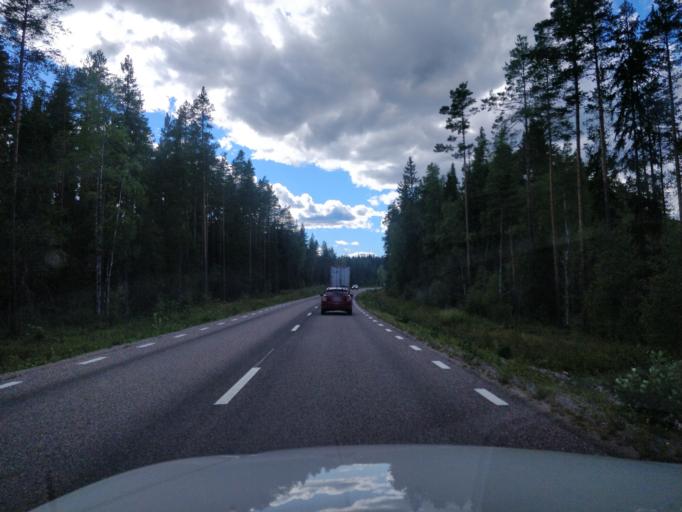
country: SE
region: Dalarna
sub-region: Ludvika Kommun
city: Abborrberget
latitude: 60.1857
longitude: 14.7924
